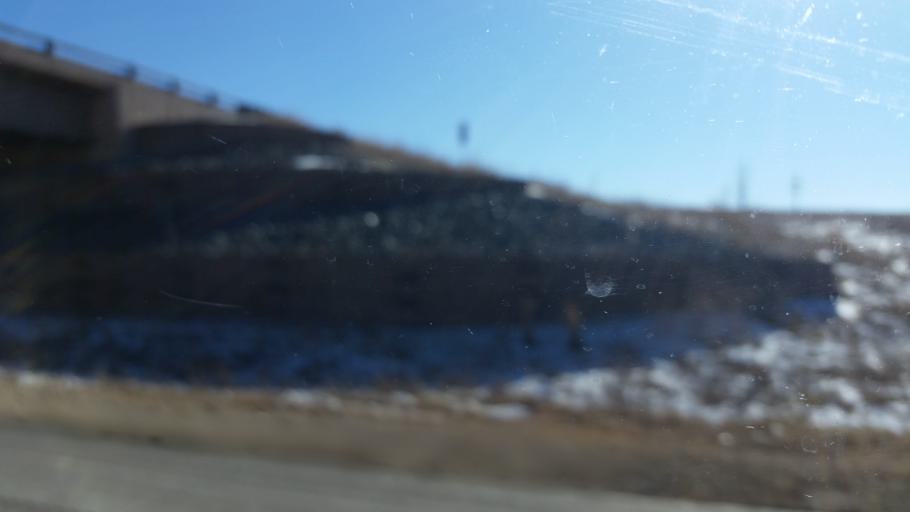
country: US
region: Colorado
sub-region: Weld County
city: Windsor
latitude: 40.4064
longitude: -104.8704
